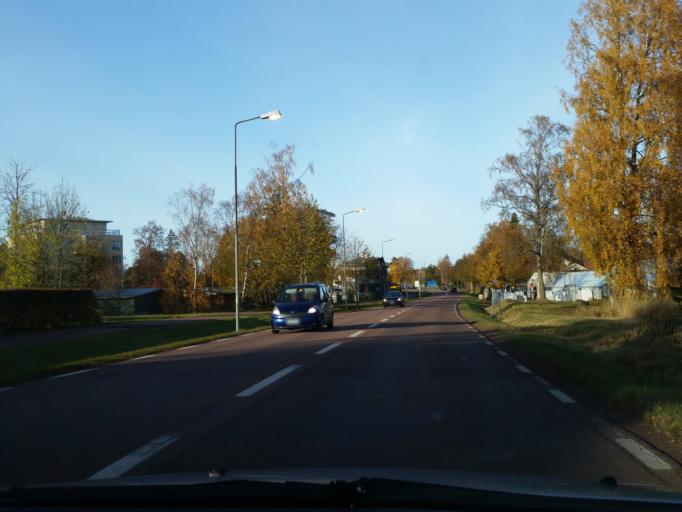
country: AX
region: Mariehamns stad
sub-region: Mariehamn
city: Mariehamn
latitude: 60.1087
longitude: 19.9306
